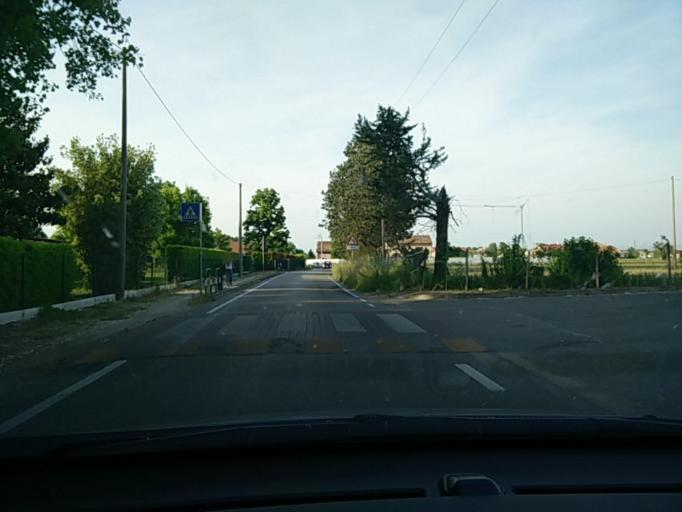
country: IT
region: Veneto
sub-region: Provincia di Padova
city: Sarmeola
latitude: 45.4215
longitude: 11.8399
